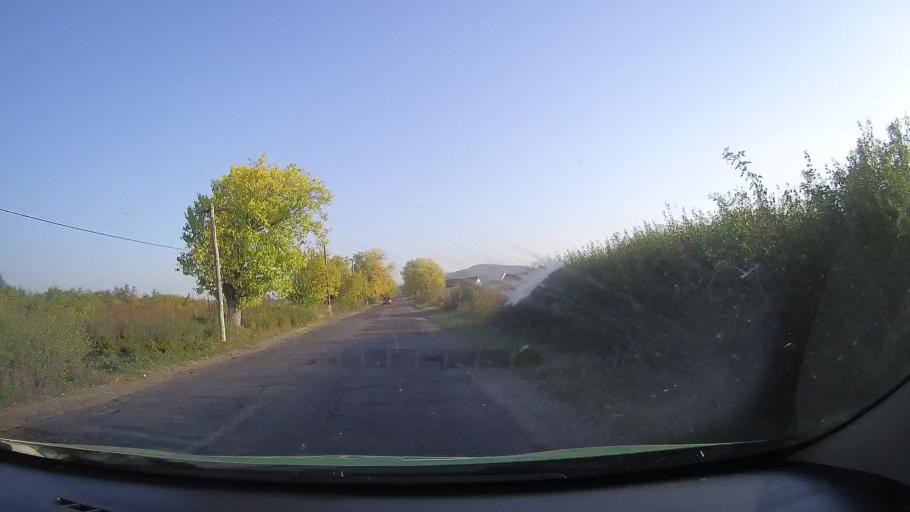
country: RO
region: Arad
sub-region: Comuna Pancota
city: Maderat
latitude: 46.3104
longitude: 21.7047
